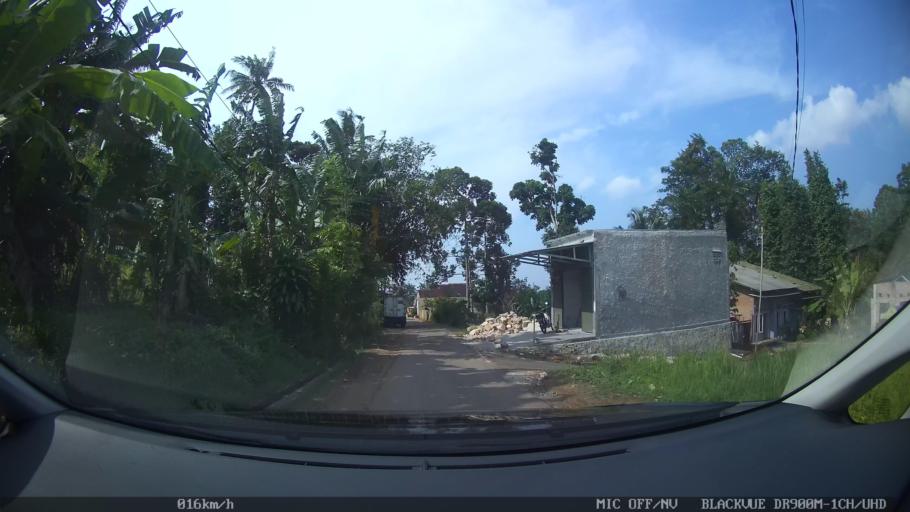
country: ID
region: Lampung
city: Kedaton
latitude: -5.3864
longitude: 105.2301
